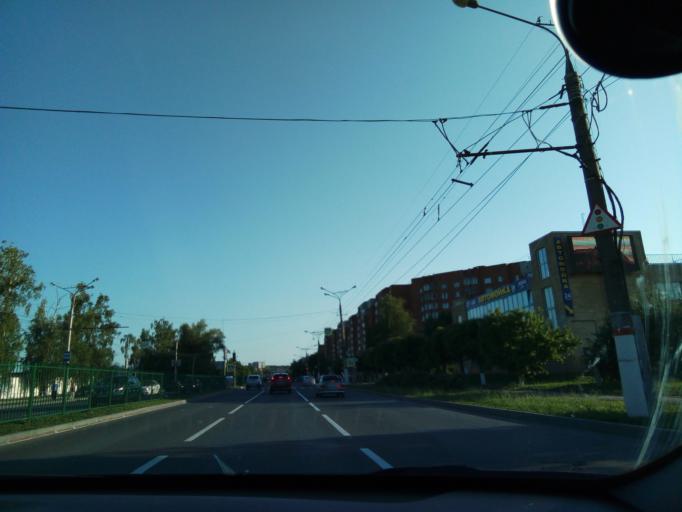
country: RU
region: Chuvashia
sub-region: Cheboksarskiy Rayon
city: Cheboksary
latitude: 56.1164
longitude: 47.2741
